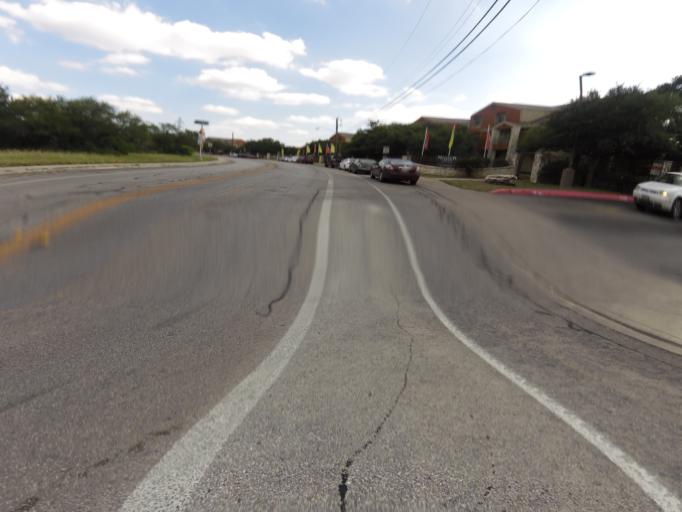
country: US
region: Texas
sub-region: Bexar County
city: Cross Mountain
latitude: 29.5918
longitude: -98.6253
